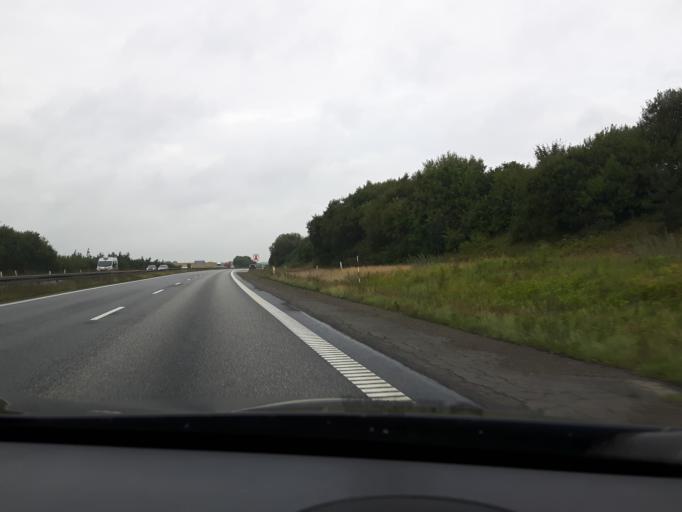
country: DK
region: North Denmark
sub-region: Mariagerfjord Kommune
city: Hobro
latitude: 56.5913
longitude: 9.7699
